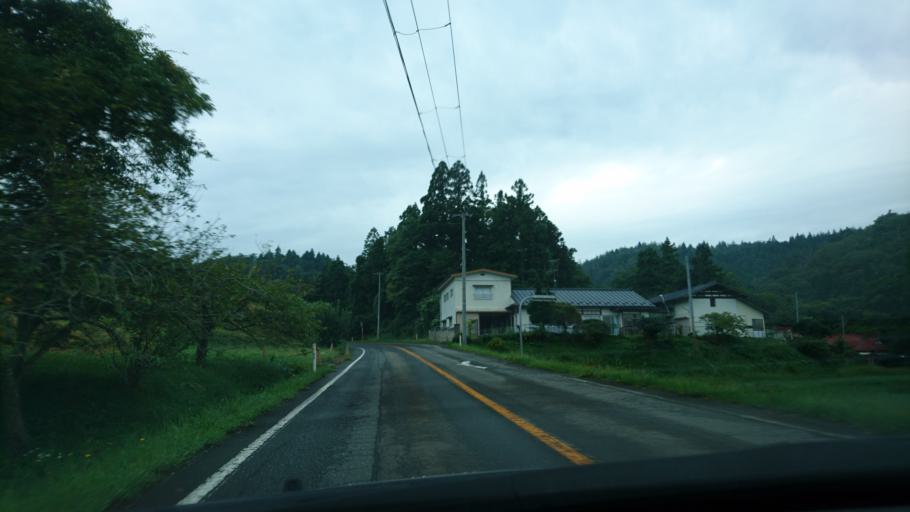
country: JP
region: Iwate
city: Ichinoseki
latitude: 39.0179
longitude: 141.2335
